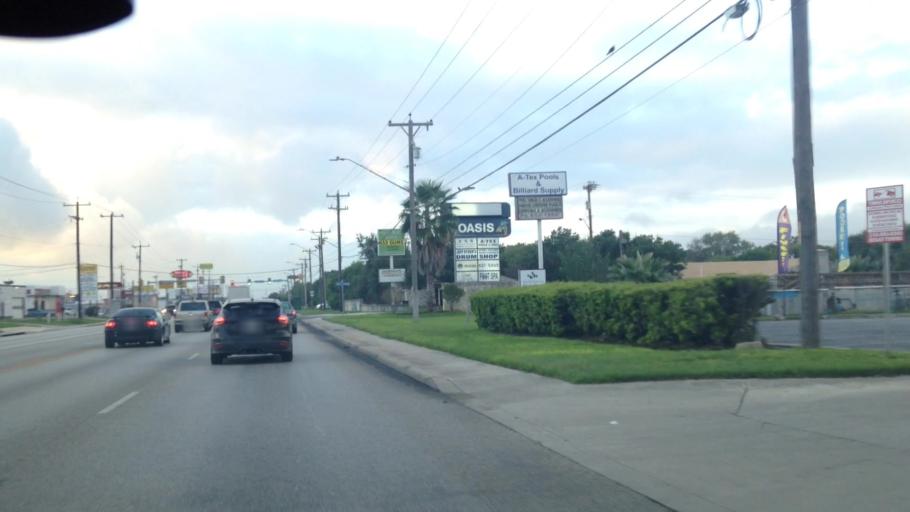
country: US
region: Texas
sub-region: Bexar County
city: Windcrest
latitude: 29.5252
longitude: -98.4111
